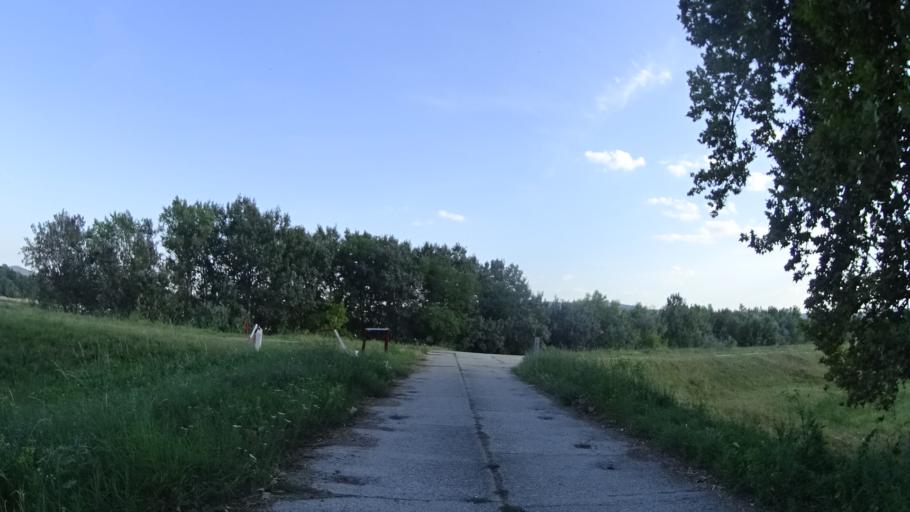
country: HU
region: Komarom-Esztergom
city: Nyergesujfalu
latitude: 47.7625
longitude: 18.5269
